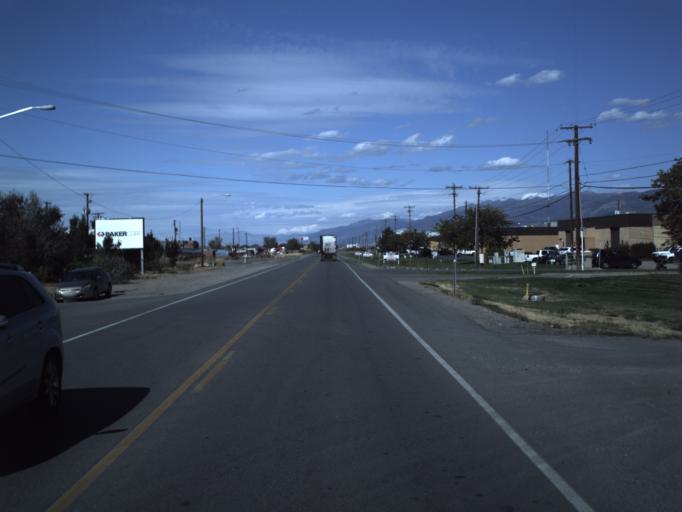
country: US
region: Utah
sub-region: Davis County
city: North Salt Lake
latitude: 40.8116
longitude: -111.9387
